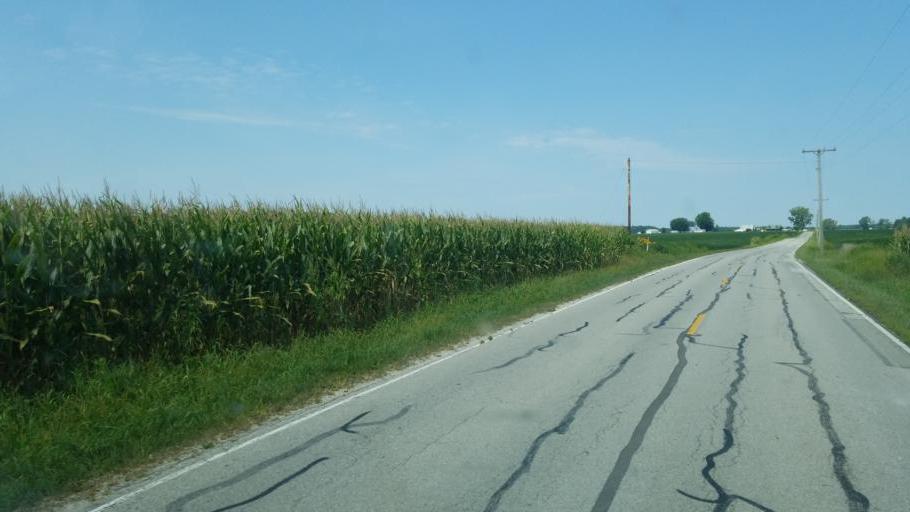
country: US
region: Ohio
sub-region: Marion County
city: Marion
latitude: 40.6655
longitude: -83.2284
